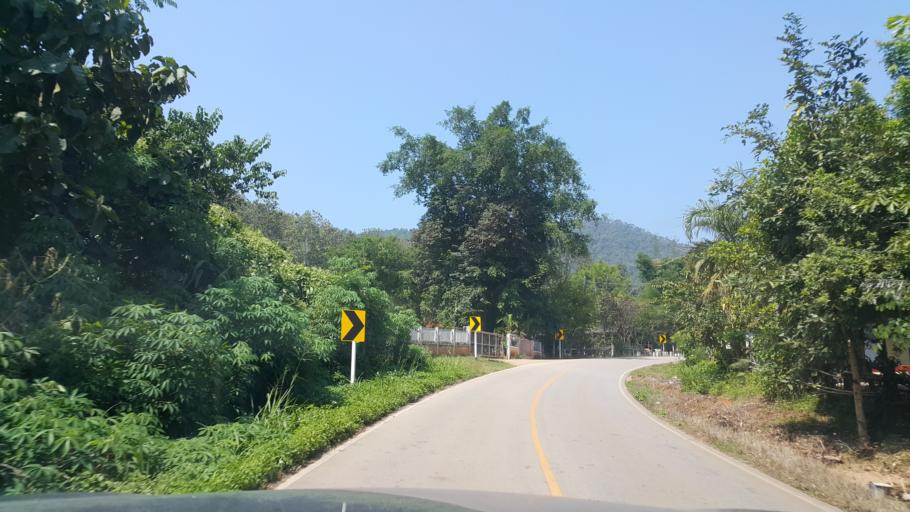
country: TH
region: Chiang Mai
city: Samoeng
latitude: 18.8662
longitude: 98.7211
